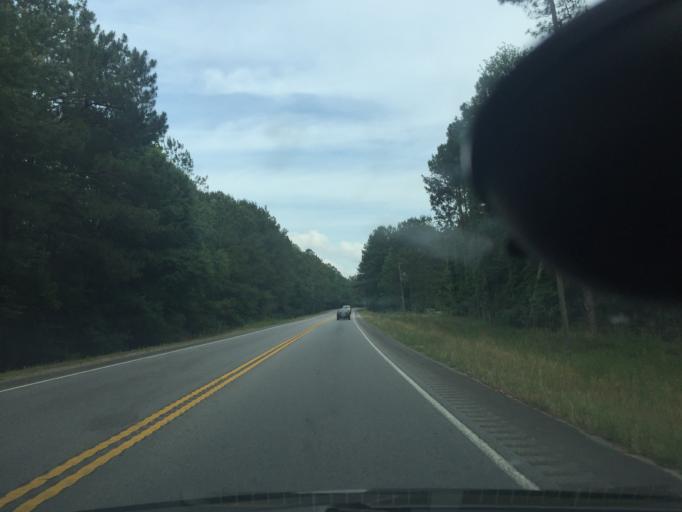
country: US
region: Georgia
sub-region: Bryan County
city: Richmond Hill
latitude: 32.0164
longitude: -81.3053
